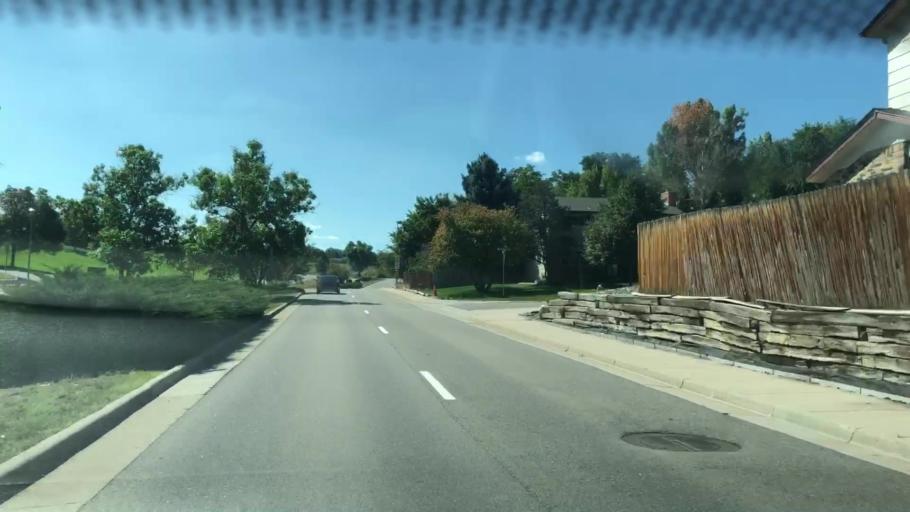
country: US
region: Colorado
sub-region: Douglas County
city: Acres Green
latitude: 39.5602
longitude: -104.8967
